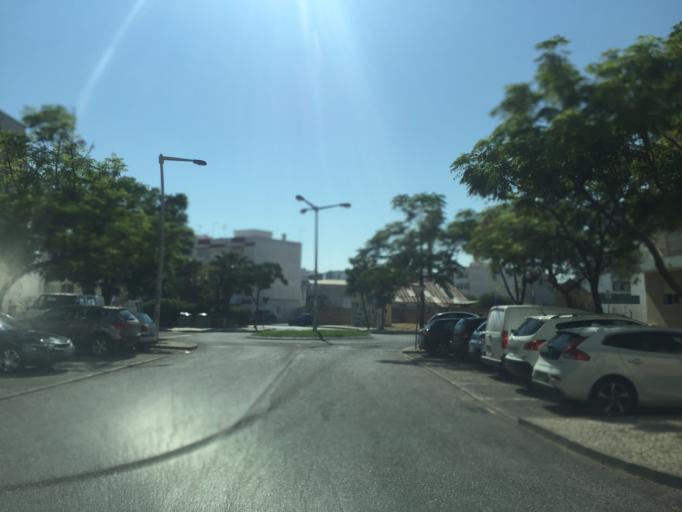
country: PT
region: Faro
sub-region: Olhao
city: Olhao
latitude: 37.0350
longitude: -7.8321
